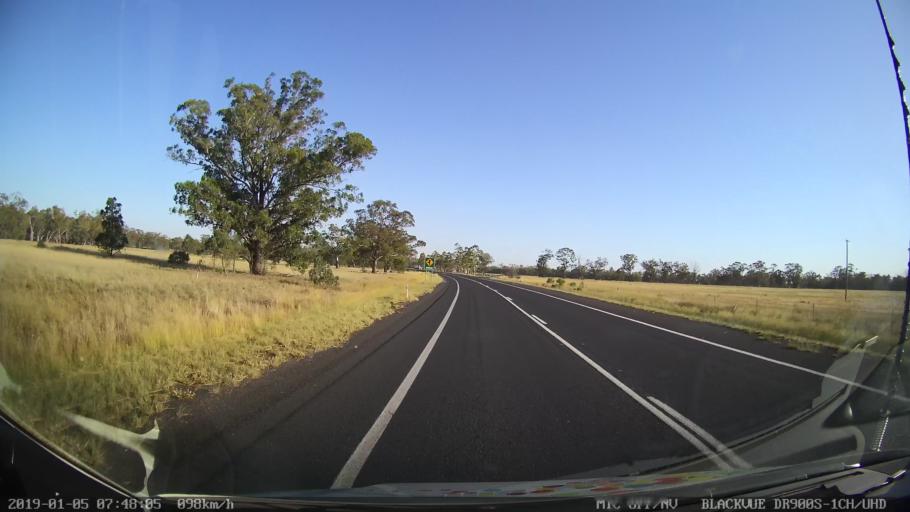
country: AU
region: New South Wales
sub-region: Gilgandra
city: Gilgandra
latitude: -31.8216
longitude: 148.6391
